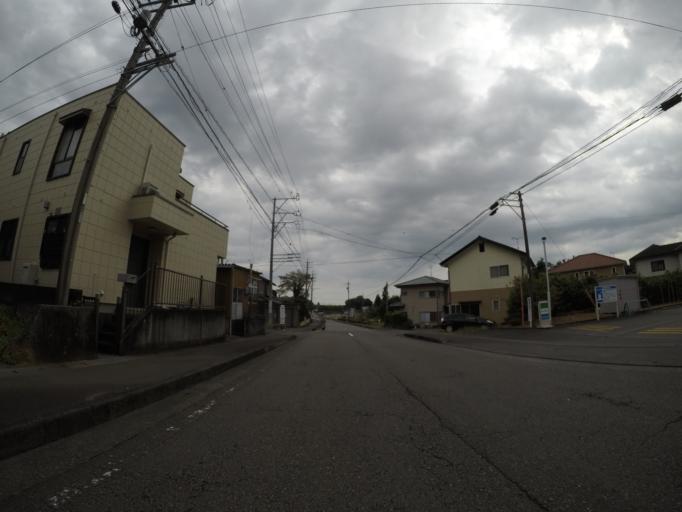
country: JP
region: Shizuoka
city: Yaizu
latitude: 34.9010
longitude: 138.2969
